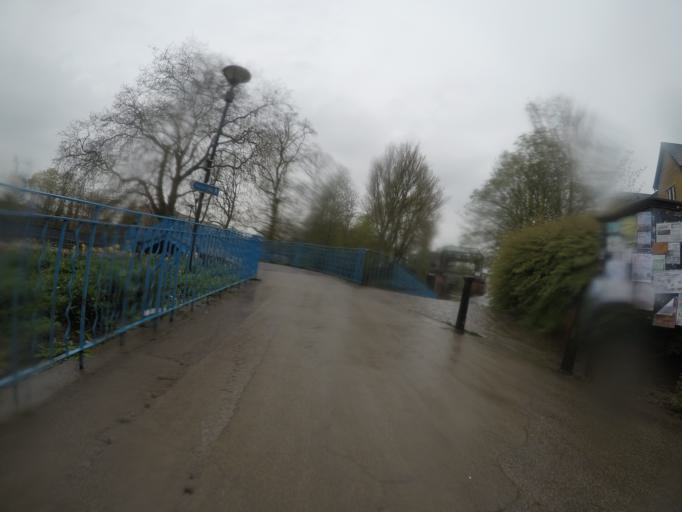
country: GB
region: England
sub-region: City of York
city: York
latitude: 53.9515
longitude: -1.0781
